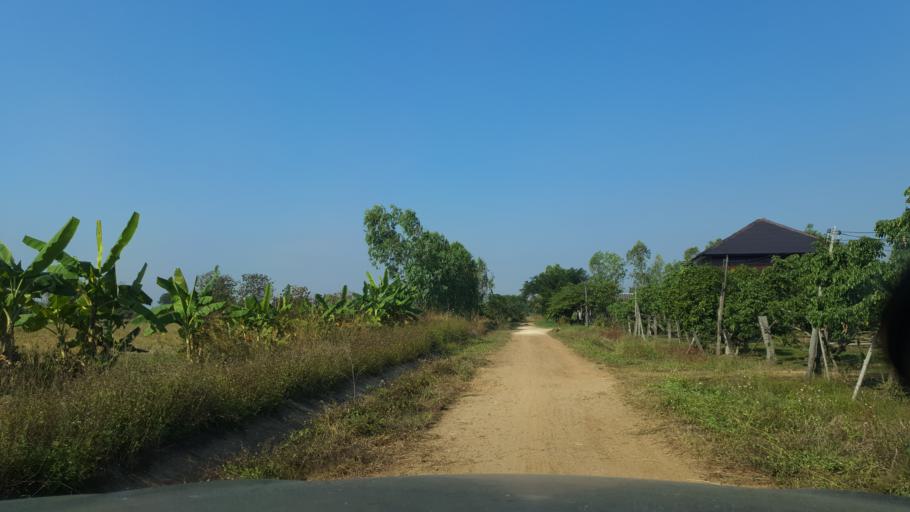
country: TH
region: Lamphun
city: Ban Thi
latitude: 18.6707
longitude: 99.1280
